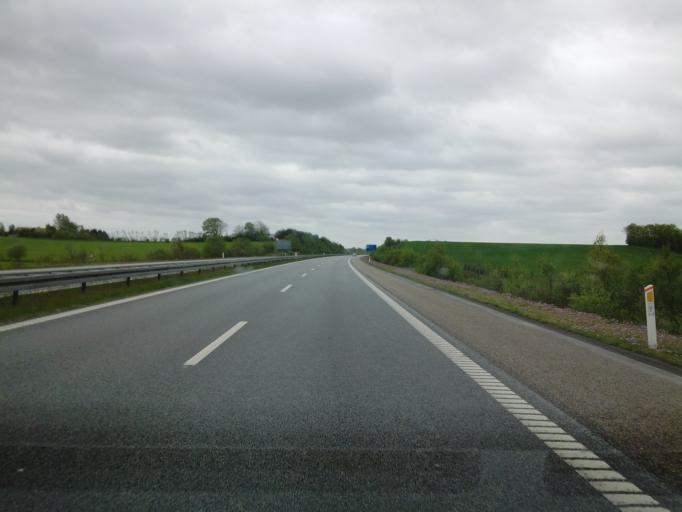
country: DK
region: North Denmark
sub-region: Bronderslev Kommune
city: Hjallerup
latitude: 57.1808
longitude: 10.1965
